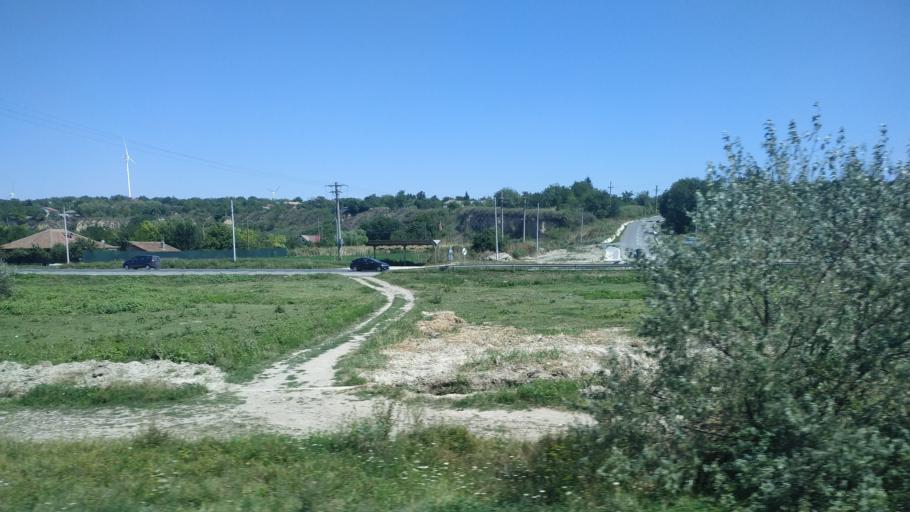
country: RO
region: Constanta
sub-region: Comuna Saligny
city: Saligny
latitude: 44.2785
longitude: 28.0841
